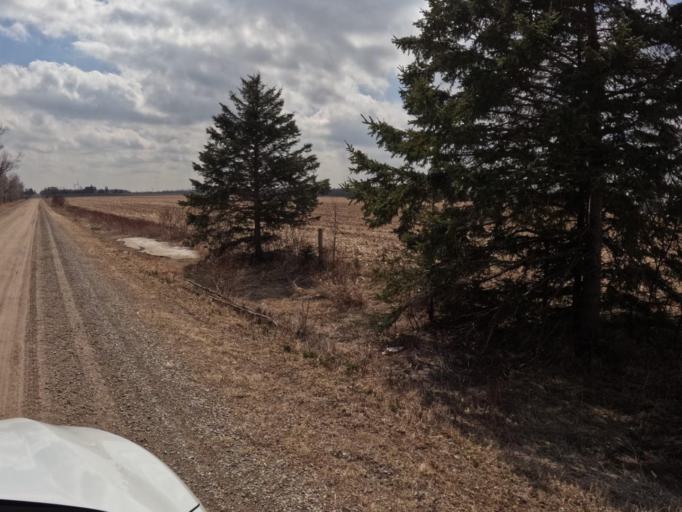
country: CA
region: Ontario
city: Shelburne
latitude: 44.0277
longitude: -80.3313
